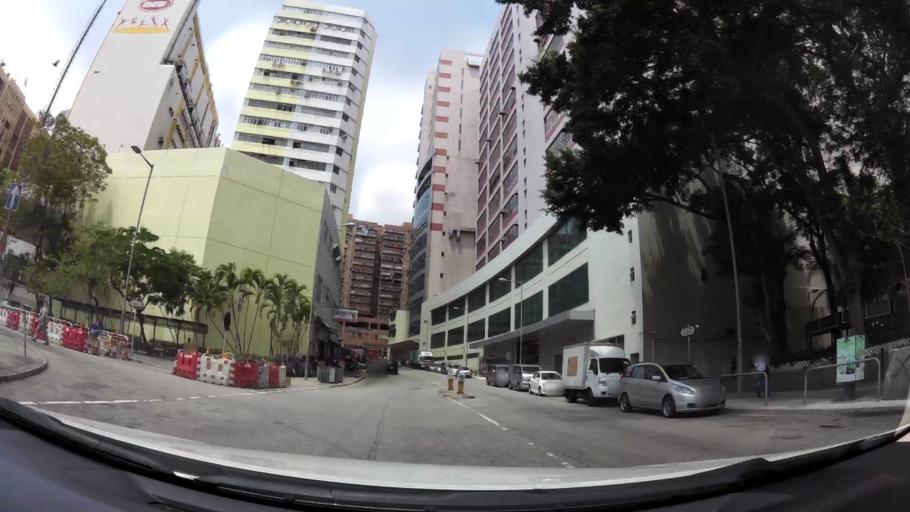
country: HK
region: Tuen Mun
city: Tuen Mun
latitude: 22.3981
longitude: 113.9696
